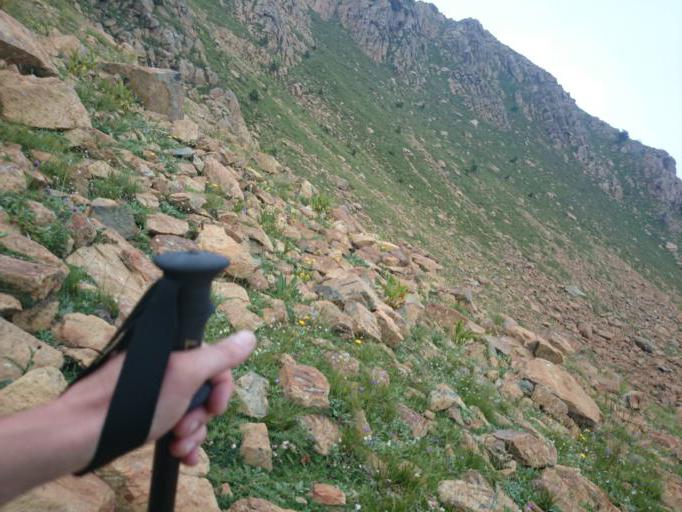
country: AL
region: Diber
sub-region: Rrethi i Dibres
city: Fushe-Lure
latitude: 41.7825
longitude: 20.1834
